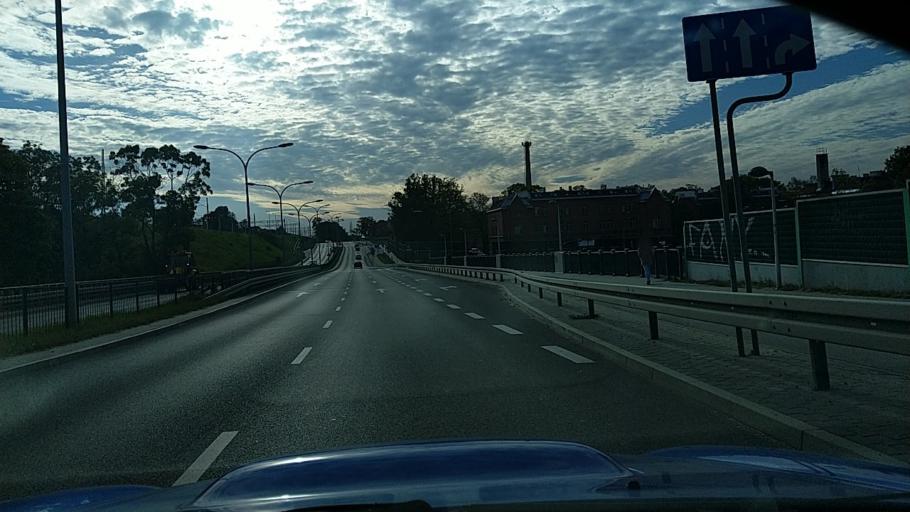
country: PL
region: Warmian-Masurian Voivodeship
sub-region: Powiat olsztynski
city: Olsztyn
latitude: 53.7808
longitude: 20.4738
